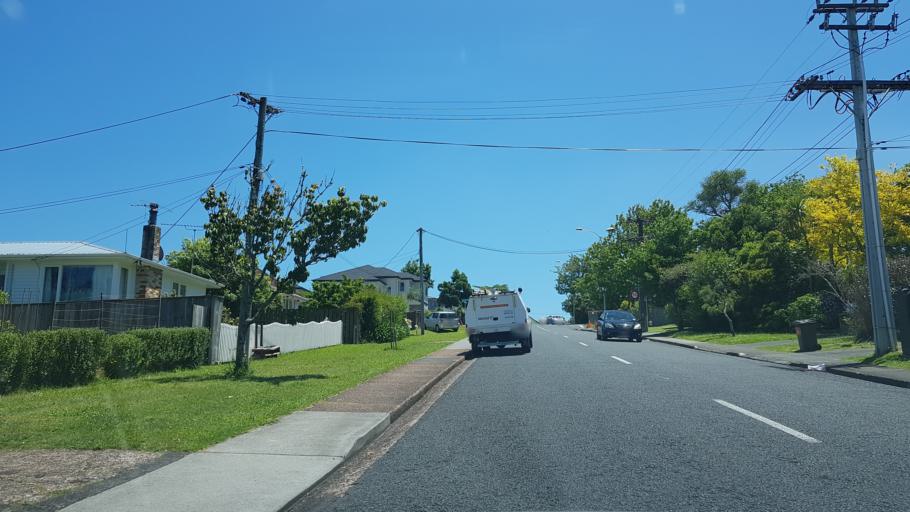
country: NZ
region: Auckland
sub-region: Auckland
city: North Shore
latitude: -36.7912
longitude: 174.7400
